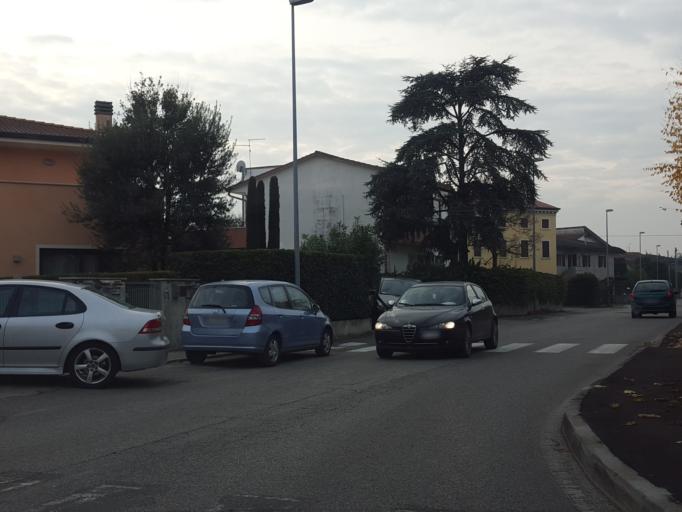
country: IT
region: Veneto
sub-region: Provincia di Verona
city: San Bonifacio
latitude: 45.3985
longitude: 11.2878
